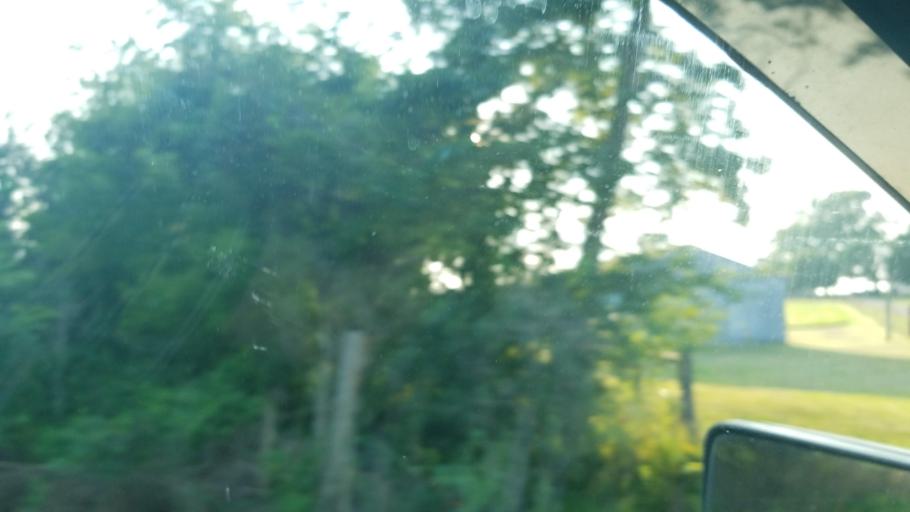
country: US
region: Illinois
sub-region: Saline County
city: Harrisburg
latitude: 37.7944
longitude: -88.6056
